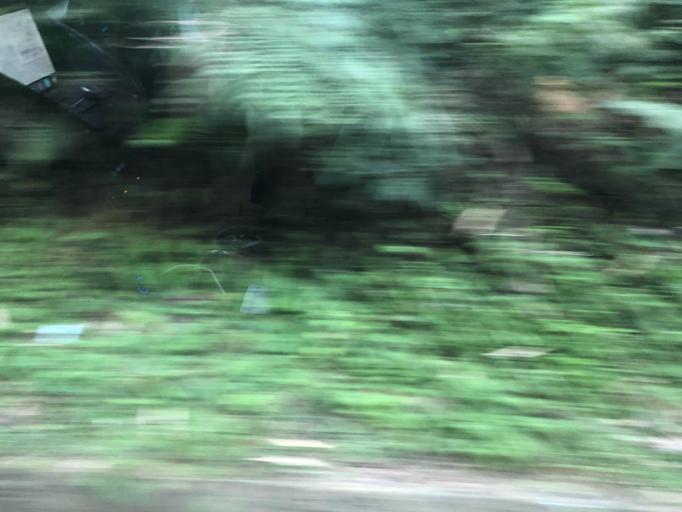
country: TW
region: Taiwan
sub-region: Taoyuan
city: Taoyuan
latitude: 24.9247
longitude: 121.3806
